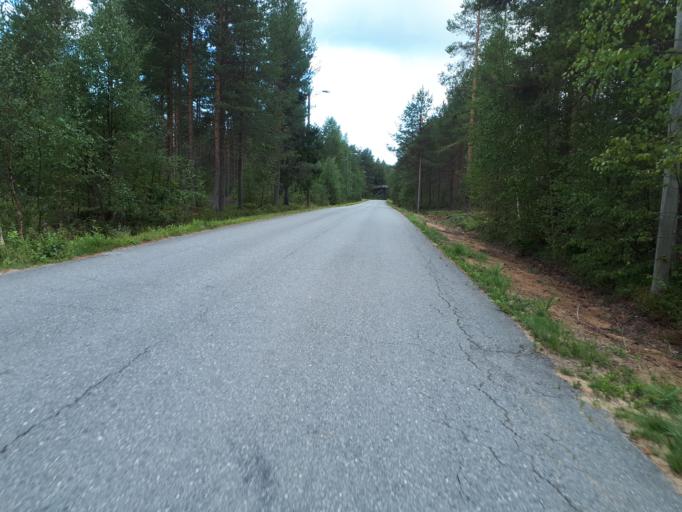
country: FI
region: Northern Ostrobothnia
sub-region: Oulunkaari
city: Ii
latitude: 65.3295
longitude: 25.3954
